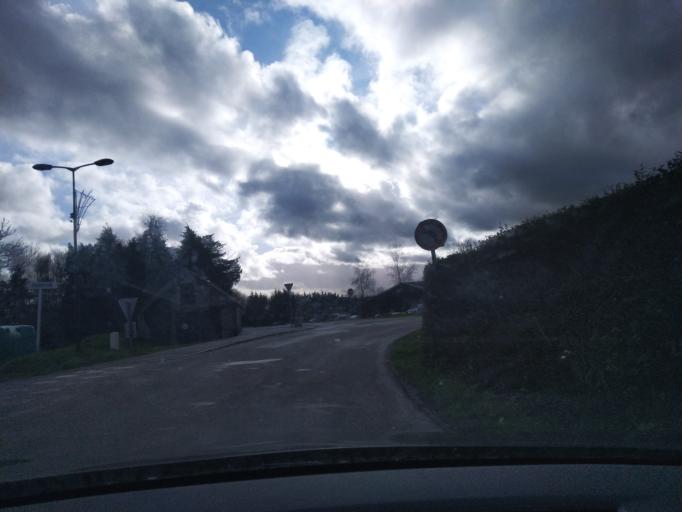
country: FR
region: Brittany
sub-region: Departement du Finistere
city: Guerlesquin
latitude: 48.4436
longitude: -3.5847
